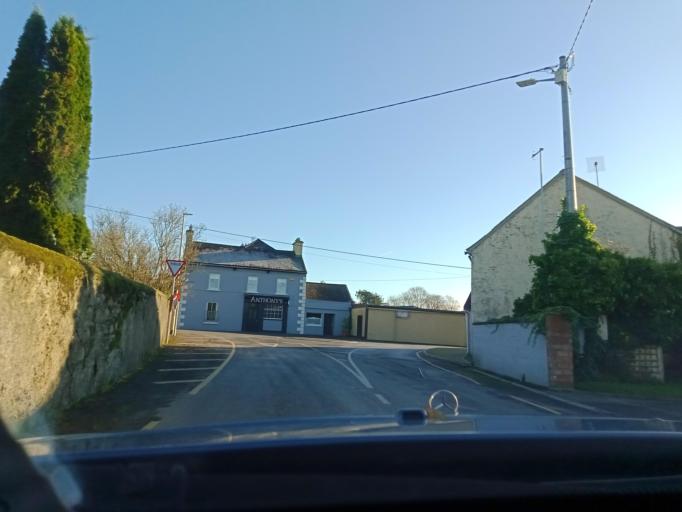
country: IE
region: Leinster
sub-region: Kilkenny
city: Piltown
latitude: 52.3878
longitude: -7.3446
